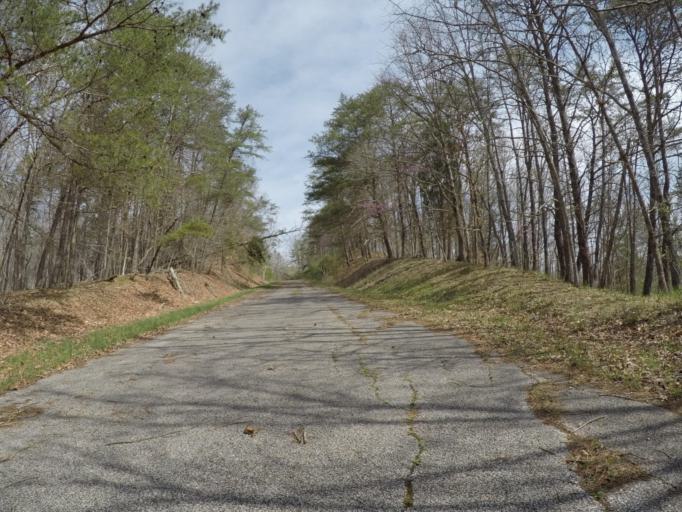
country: US
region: West Virginia
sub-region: Wayne County
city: Lavalette
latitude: 38.3125
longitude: -82.3514
